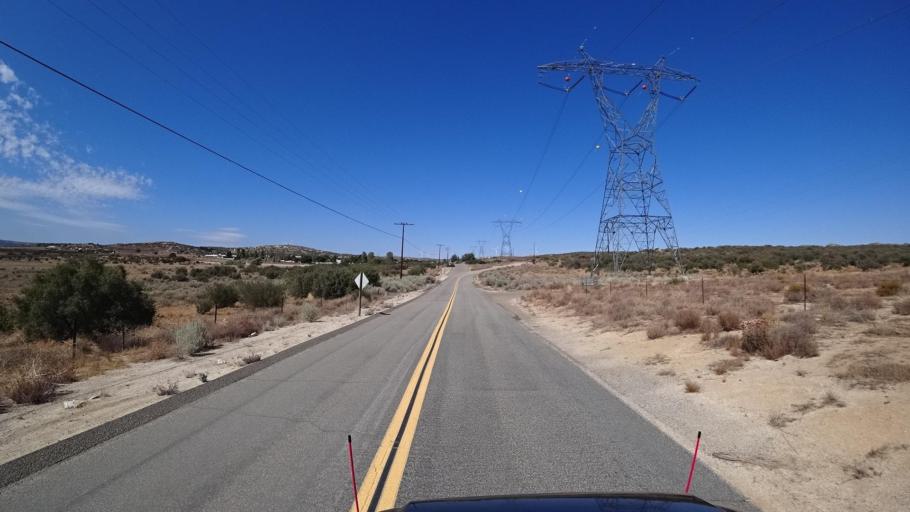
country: MX
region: Baja California
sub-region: Tecate
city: Cereso del Hongo
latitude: 32.6943
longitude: -116.2598
